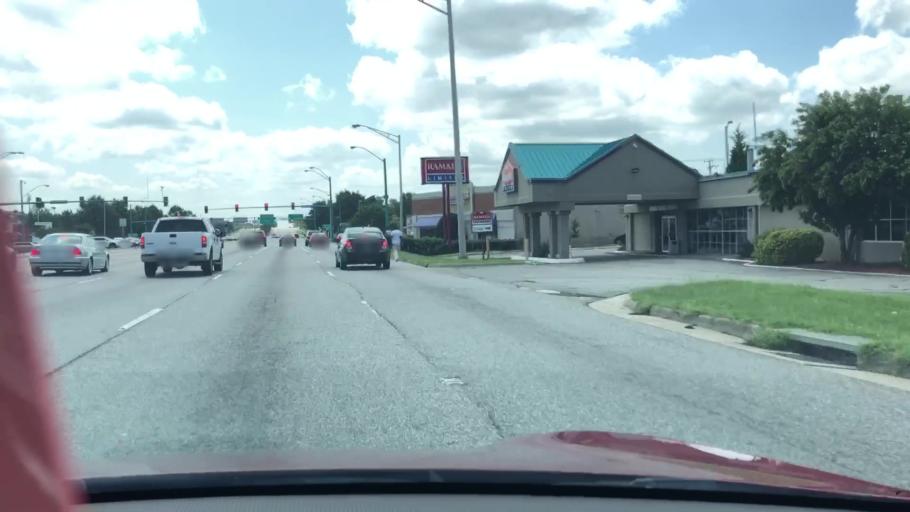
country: US
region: Virginia
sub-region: City of Chesapeake
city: Chesapeake
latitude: 36.8500
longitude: -76.2102
